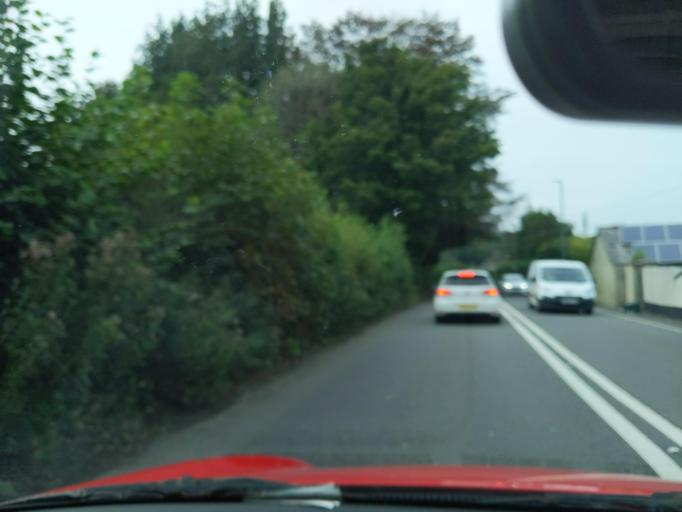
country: GB
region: England
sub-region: Devon
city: Horrabridge
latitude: 50.5007
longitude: -4.0989
